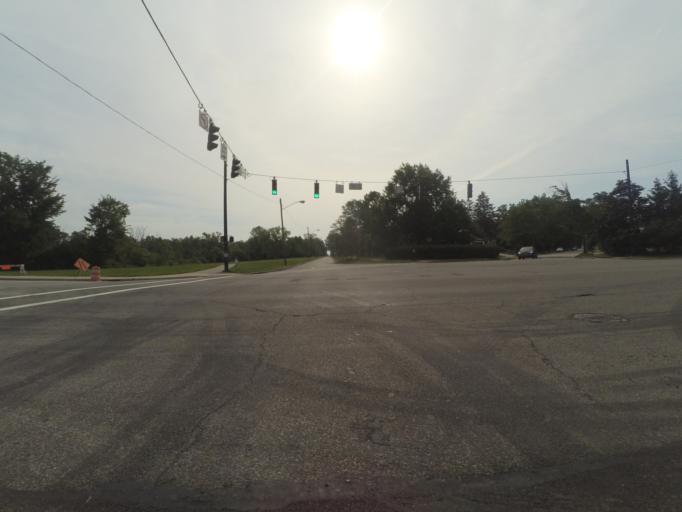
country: US
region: Ohio
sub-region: Cuyahoga County
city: Beachwood
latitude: 41.4779
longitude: -81.5171
